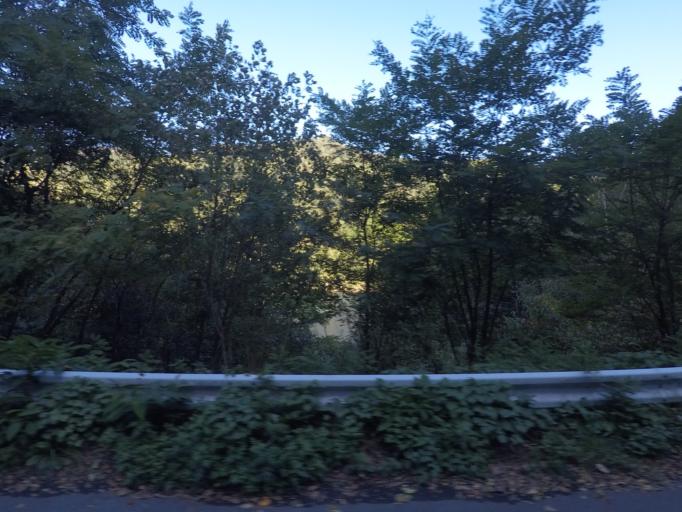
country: JP
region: Nagano
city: Shiojiri
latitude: 36.0006
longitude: 137.7695
